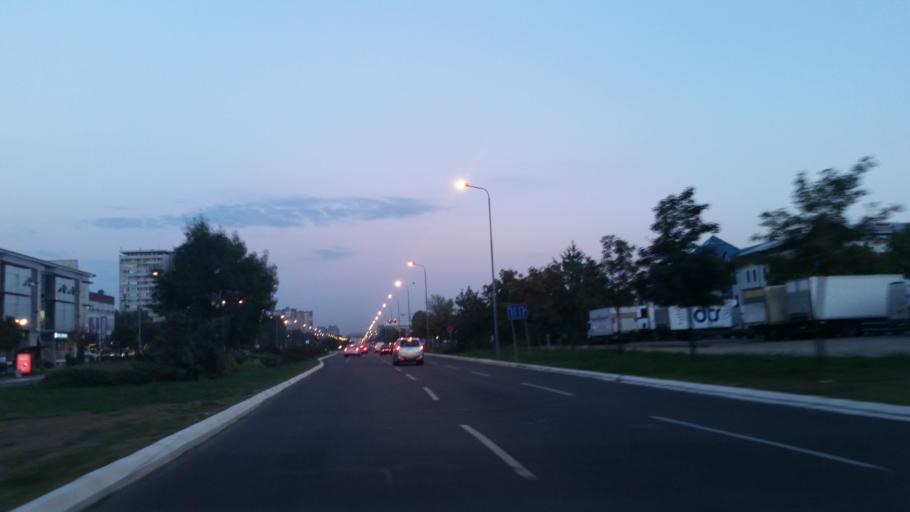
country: RS
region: Central Serbia
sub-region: Belgrade
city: Zemun
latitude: 44.8176
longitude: 20.3988
